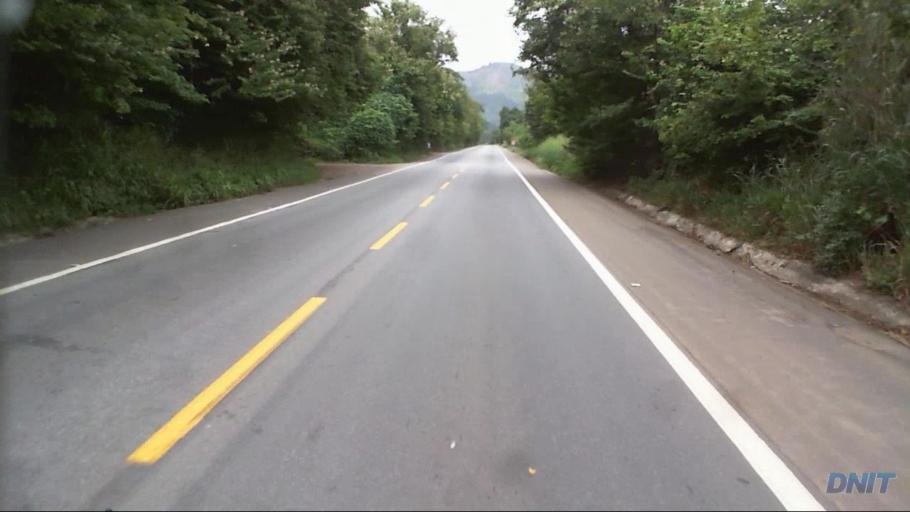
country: BR
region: Minas Gerais
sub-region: Timoteo
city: Timoteo
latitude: -19.5516
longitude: -42.7050
